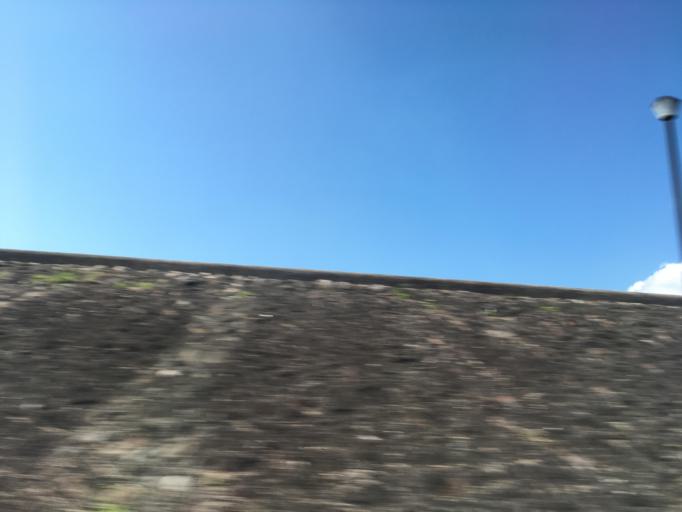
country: TW
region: Taiwan
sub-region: Yilan
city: Yilan
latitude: 24.7548
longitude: 121.7323
